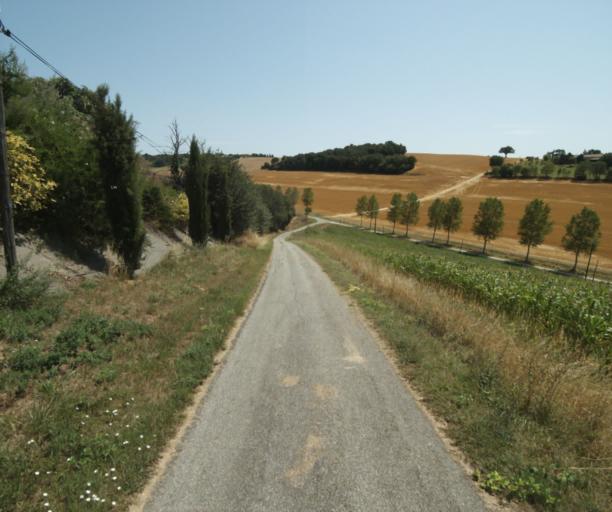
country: FR
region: Midi-Pyrenees
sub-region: Departement de la Haute-Garonne
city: Saint-Felix-Lauragais
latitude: 43.4641
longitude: 1.8619
